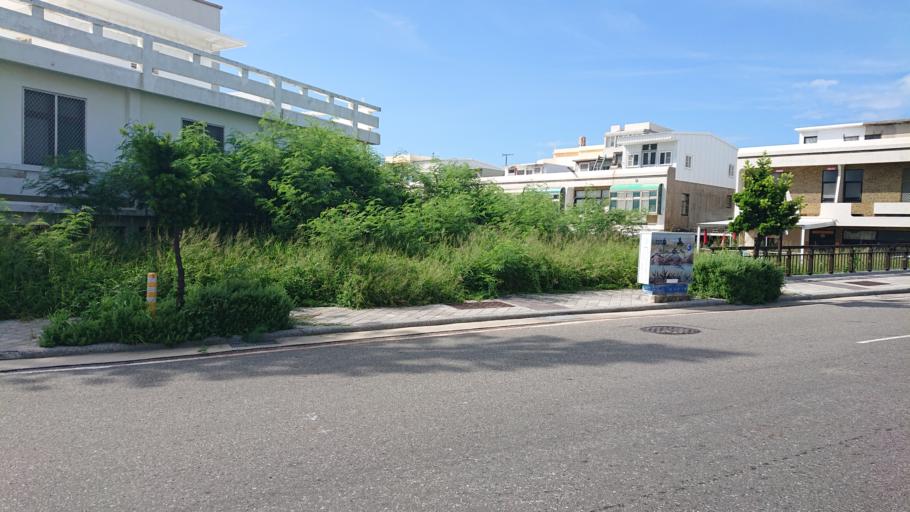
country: TW
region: Taiwan
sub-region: Penghu
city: Ma-kung
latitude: 23.5644
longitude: 119.5867
